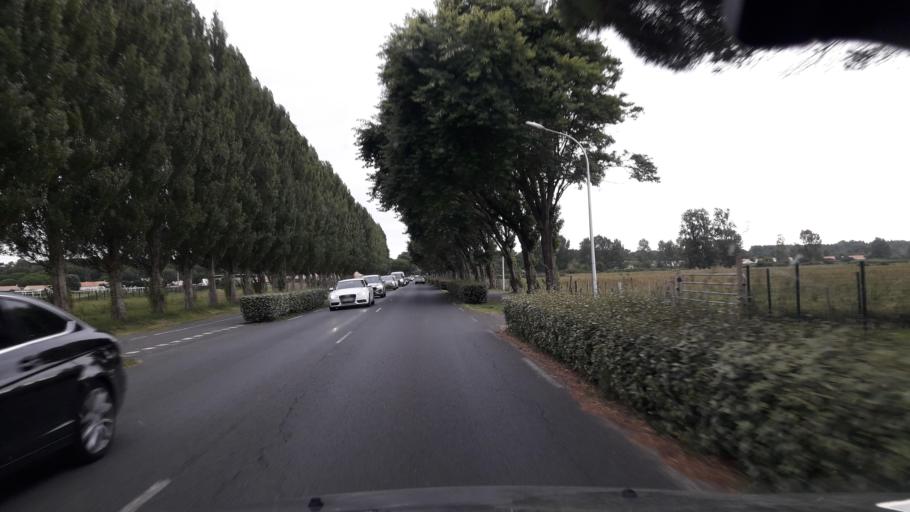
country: FR
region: Poitou-Charentes
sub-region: Departement de la Charente-Maritime
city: Les Mathes
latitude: 45.6988
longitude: -1.1725
